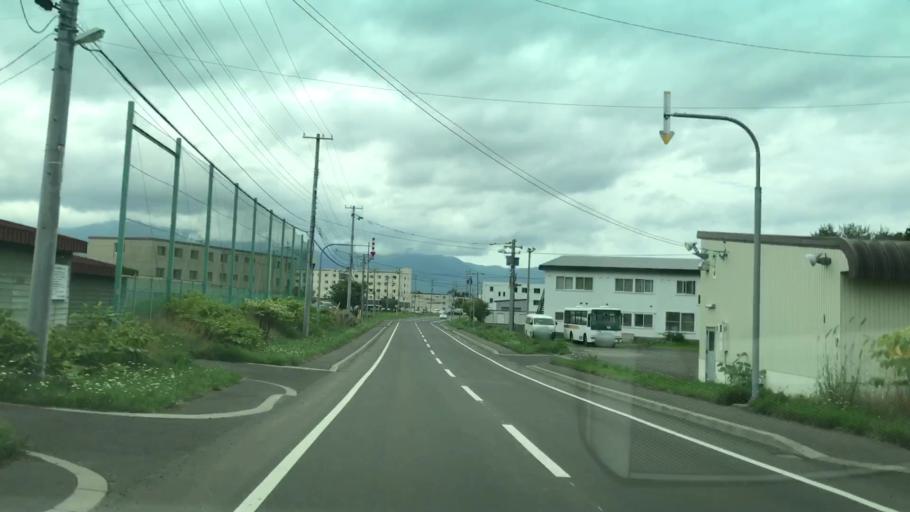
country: JP
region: Hokkaido
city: Iwanai
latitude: 43.0367
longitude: 140.5416
